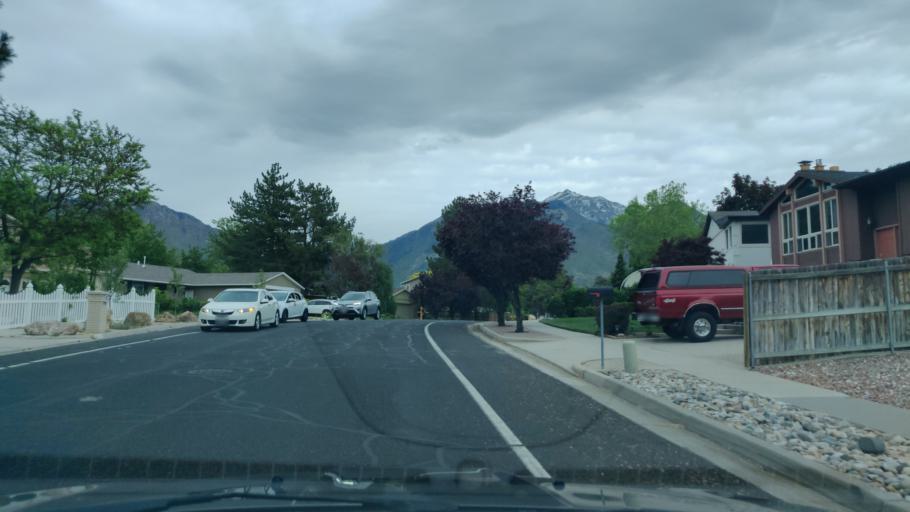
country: US
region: Utah
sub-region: Salt Lake County
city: Little Cottonwood Creek Valley
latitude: 40.6164
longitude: -111.8381
